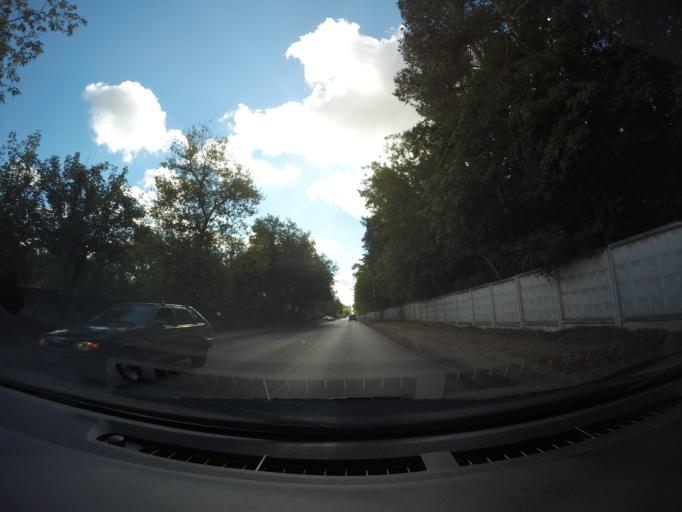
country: RU
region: Moskovskaya
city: Kratovo
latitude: 55.5875
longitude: 38.1923
